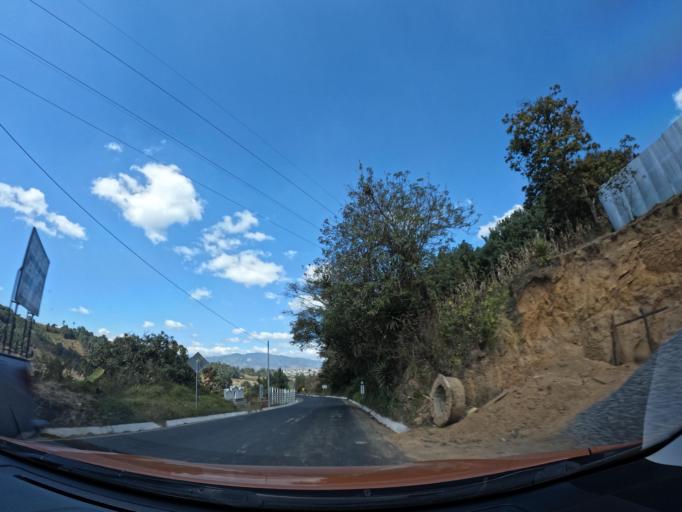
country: GT
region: Chimaltenango
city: Patzun
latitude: 14.6570
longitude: -91.0196
